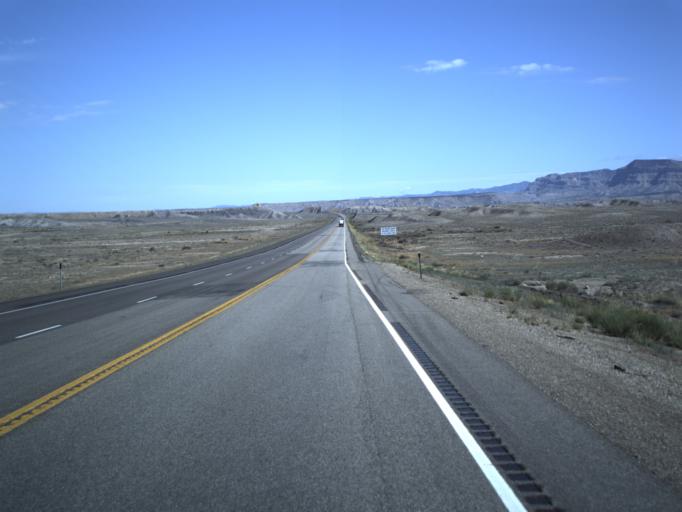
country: US
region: Utah
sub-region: Carbon County
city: East Carbon City
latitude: 39.3078
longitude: -110.3597
